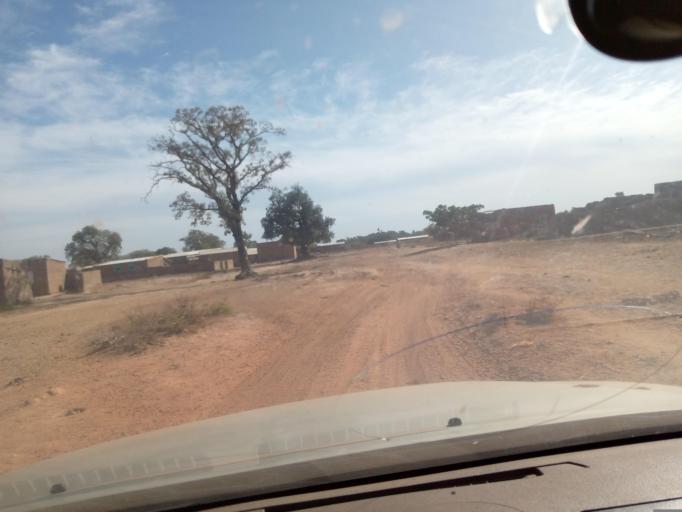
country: ML
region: Sikasso
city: Sikasso
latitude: 11.4640
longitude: -5.3238
